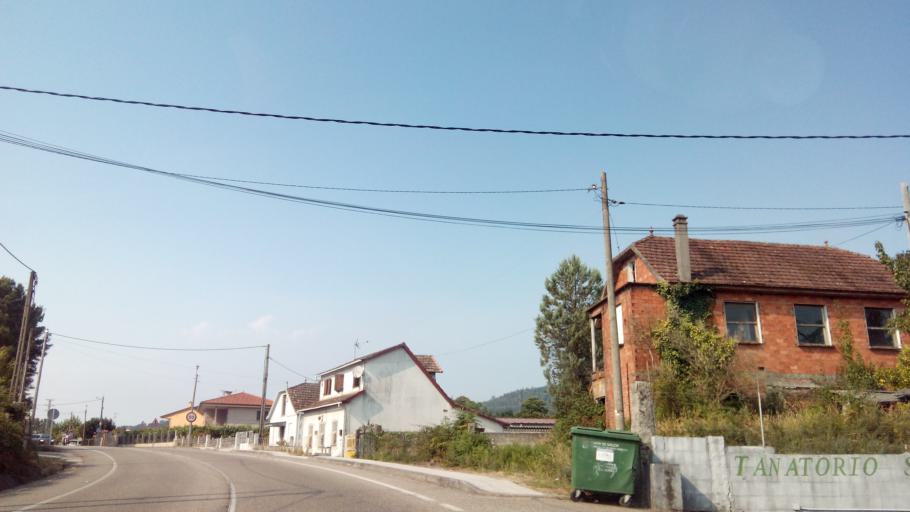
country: ES
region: Galicia
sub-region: Provincia de Pontevedra
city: Ponteareas
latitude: 42.1846
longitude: -8.5069
